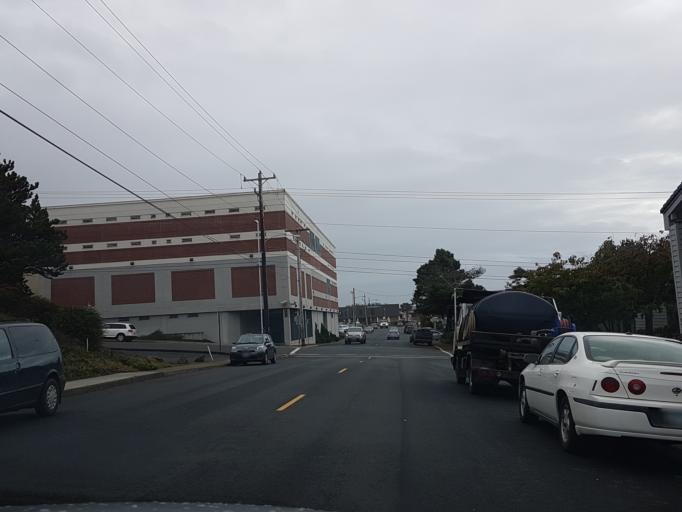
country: US
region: Oregon
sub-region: Lincoln County
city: Newport
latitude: 44.6371
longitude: -124.0557
